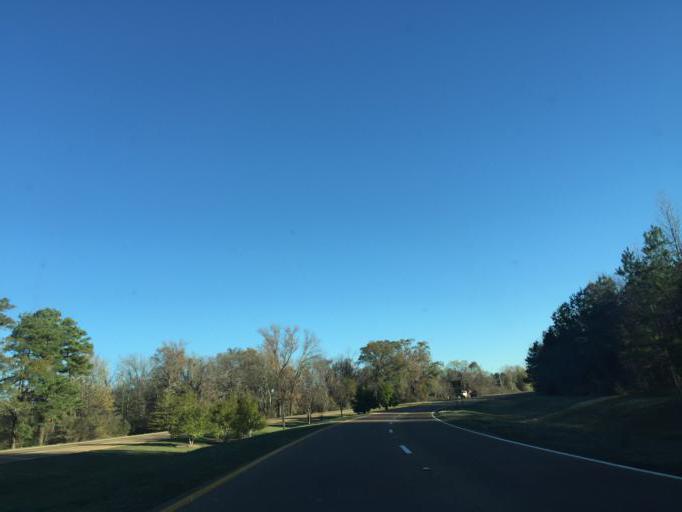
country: US
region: Mississippi
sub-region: Rankin County
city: Pearl
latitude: 32.2864
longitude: -90.1563
